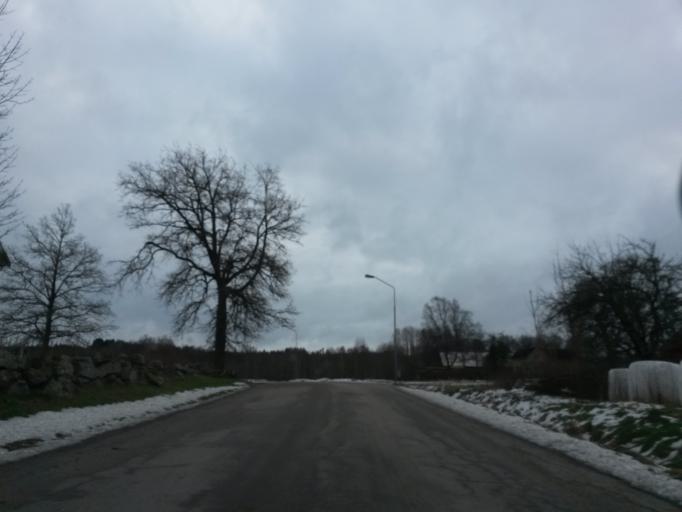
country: SE
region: Vaestra Goetaland
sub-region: Herrljunga Kommun
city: Herrljunga
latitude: 58.0725
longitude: 13.0084
